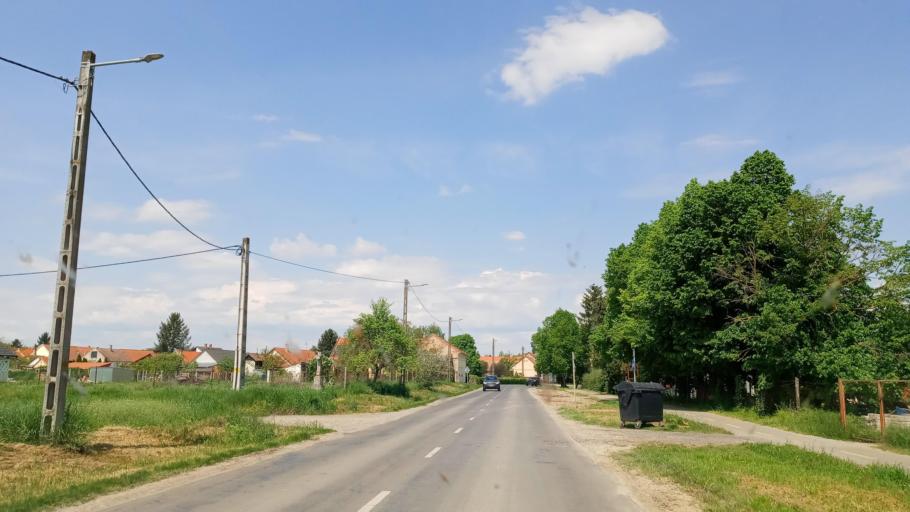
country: HU
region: Baranya
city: Boly
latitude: 45.9610
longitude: 18.5240
